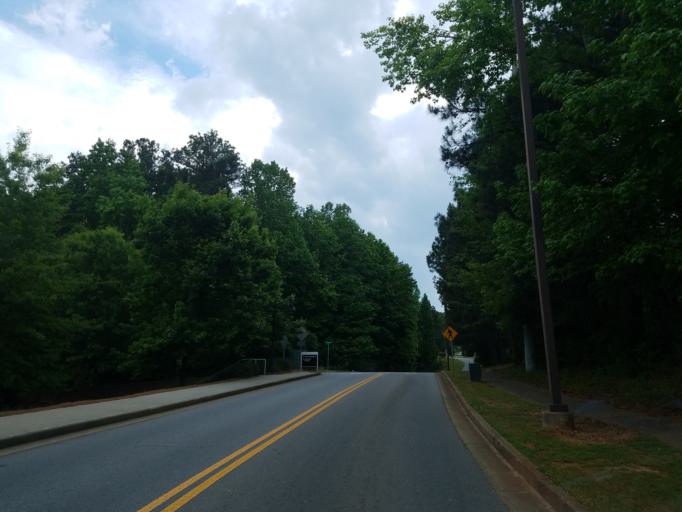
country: US
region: Georgia
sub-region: Cobb County
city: Fair Oaks
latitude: 33.9356
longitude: -84.5255
